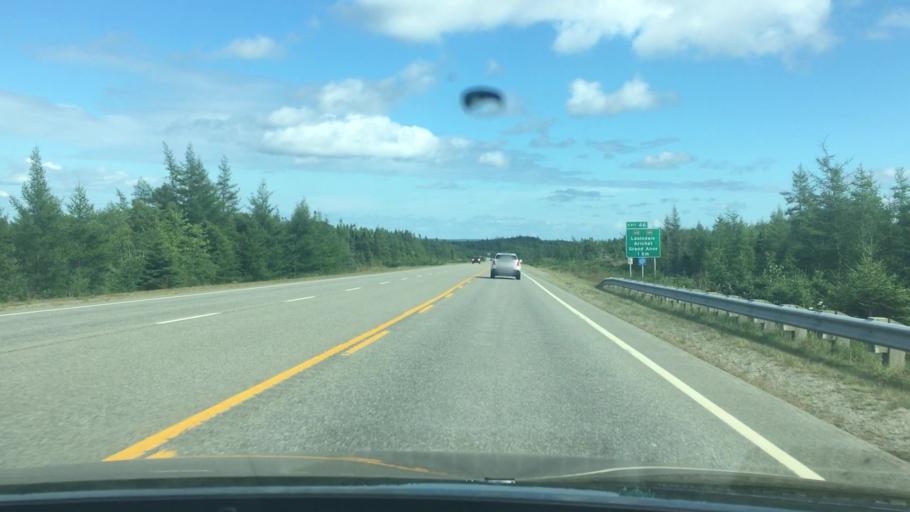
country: CA
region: Nova Scotia
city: Port Hawkesbury
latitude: 45.6185
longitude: -61.1086
